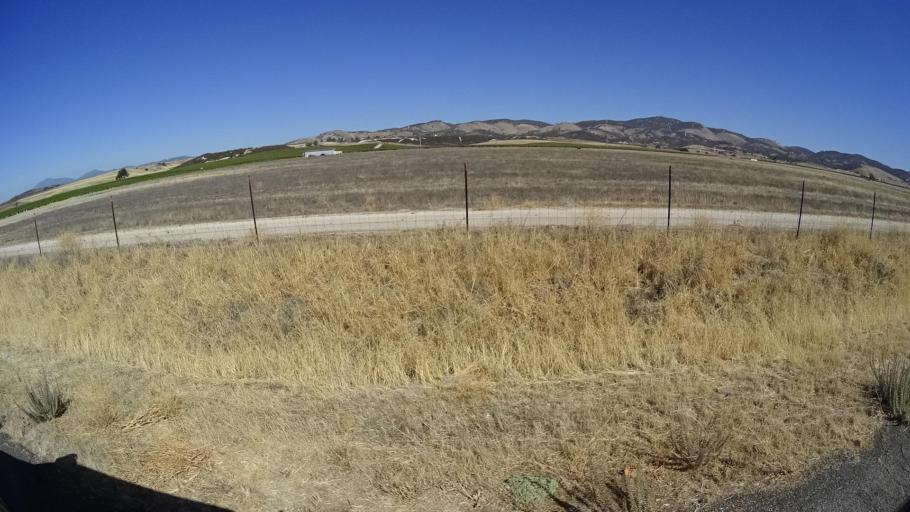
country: US
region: California
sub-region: Monterey County
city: King City
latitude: 35.9673
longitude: -121.1121
